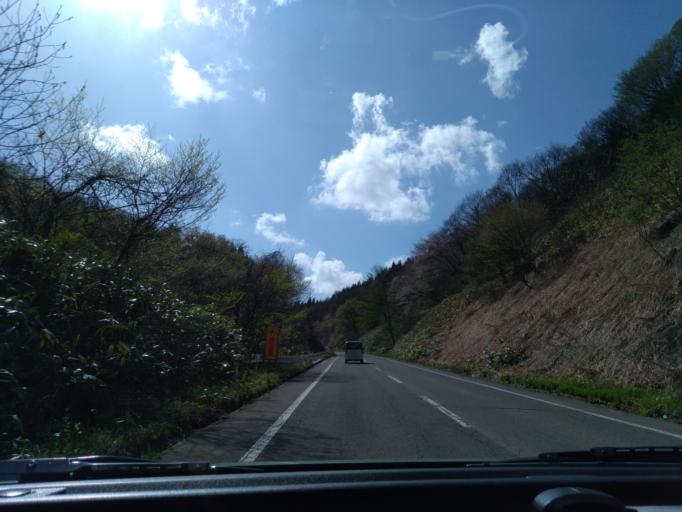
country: JP
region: Akita
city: Akita
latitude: 39.6966
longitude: 140.2573
